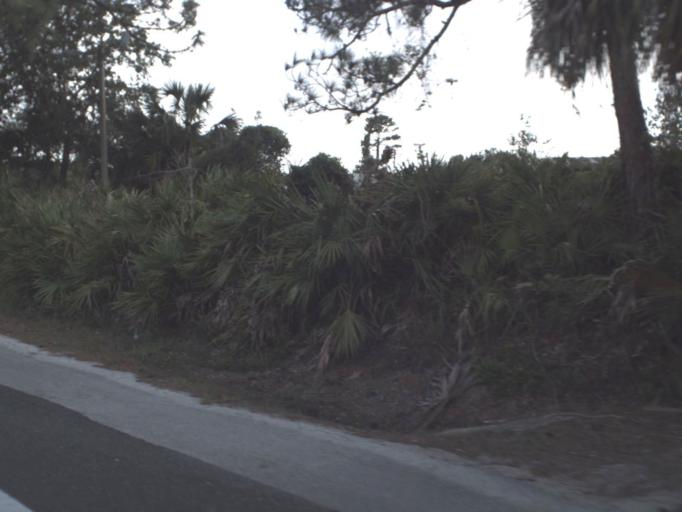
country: US
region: Florida
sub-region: Brevard County
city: Mims
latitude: 28.6985
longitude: -80.8593
